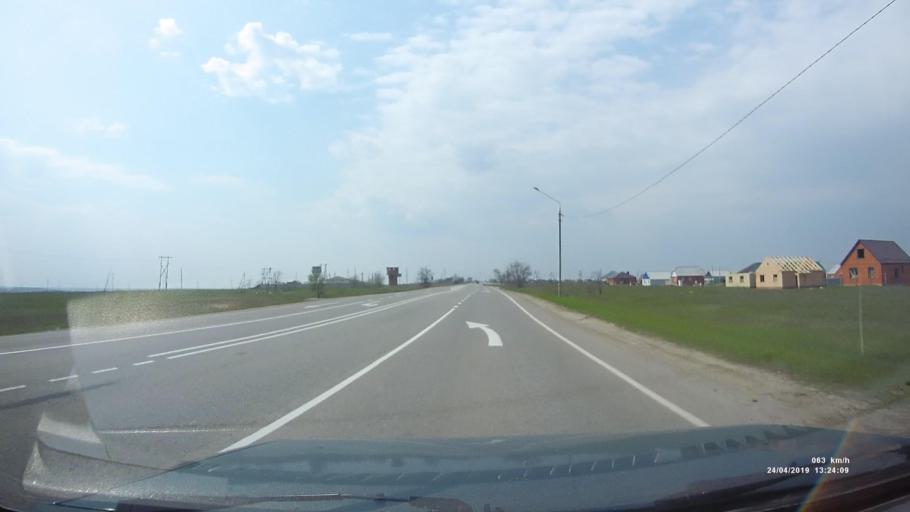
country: RU
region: Kalmykiya
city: Elista
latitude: 46.2836
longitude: 44.2594
